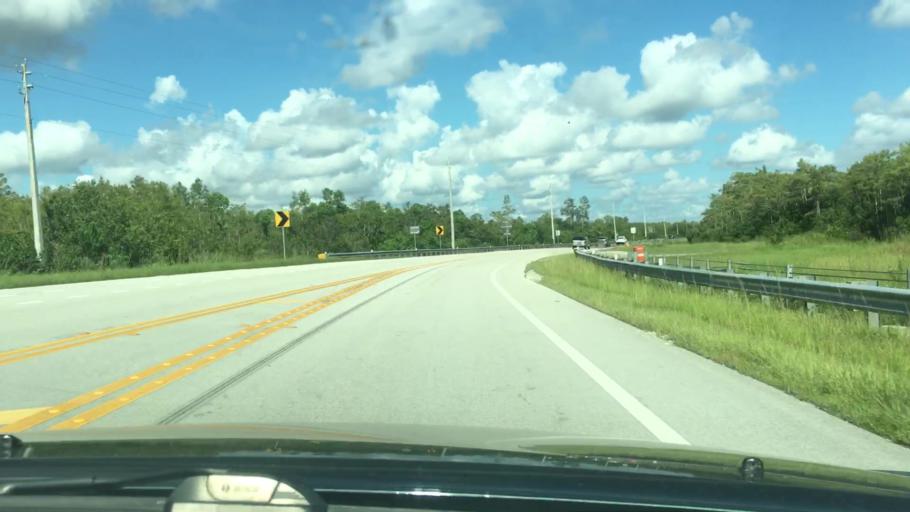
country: US
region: Florida
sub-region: Miami-Dade County
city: Kendall West
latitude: 25.7628
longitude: -80.8289
